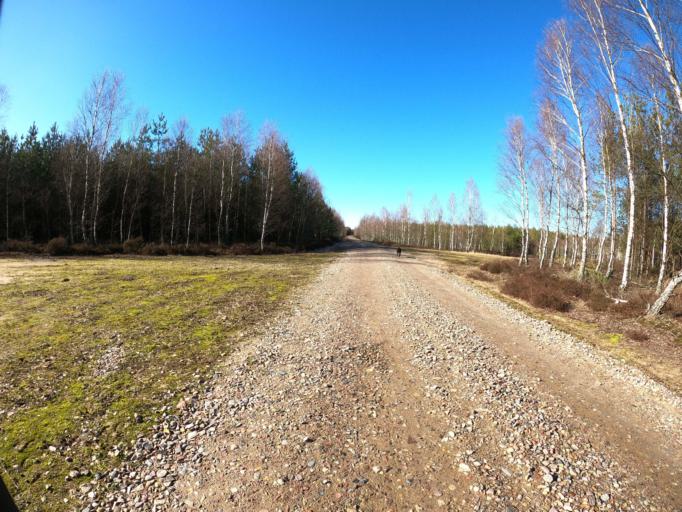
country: PL
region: Greater Poland Voivodeship
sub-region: Powiat zlotowski
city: Sypniewo
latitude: 53.5330
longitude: 16.6146
